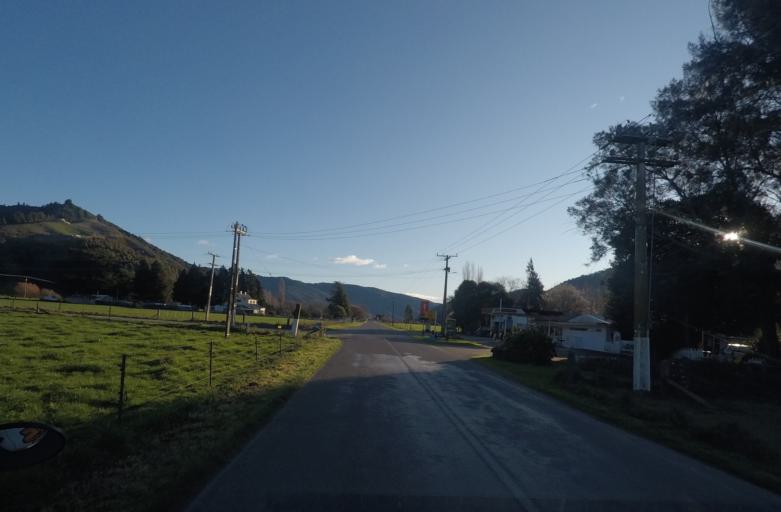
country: NZ
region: Marlborough
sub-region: Marlborough District
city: Picton
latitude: -41.2893
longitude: 173.8594
